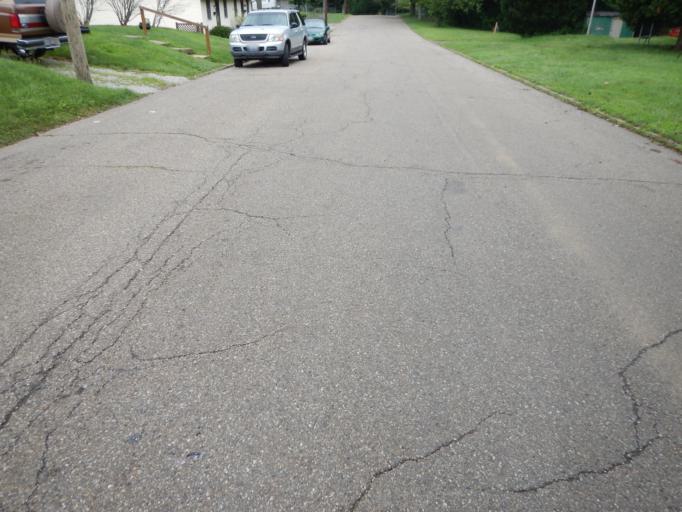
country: US
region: Ohio
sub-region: Muskingum County
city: Zanesville
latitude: 39.9332
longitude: -82.0131
